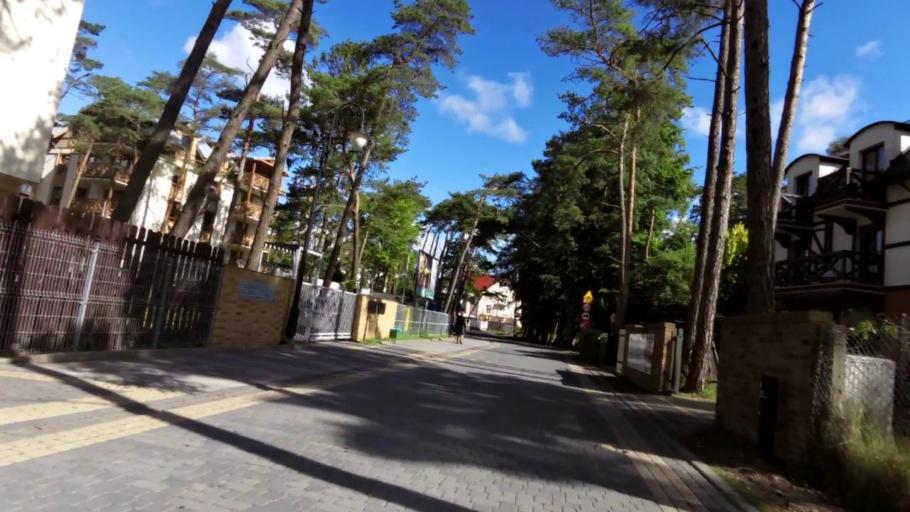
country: PL
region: West Pomeranian Voivodeship
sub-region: Powiat koszalinski
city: Mielno
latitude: 54.2616
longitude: 16.0634
